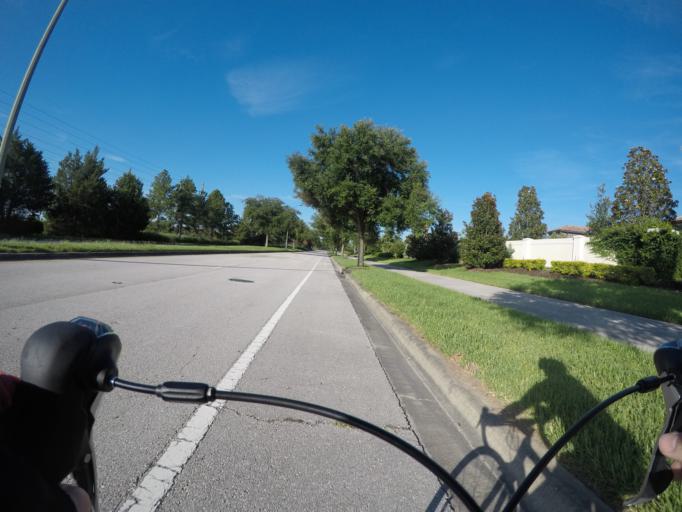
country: US
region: Florida
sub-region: Orange County
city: Meadow Woods
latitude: 28.3991
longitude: -81.2503
